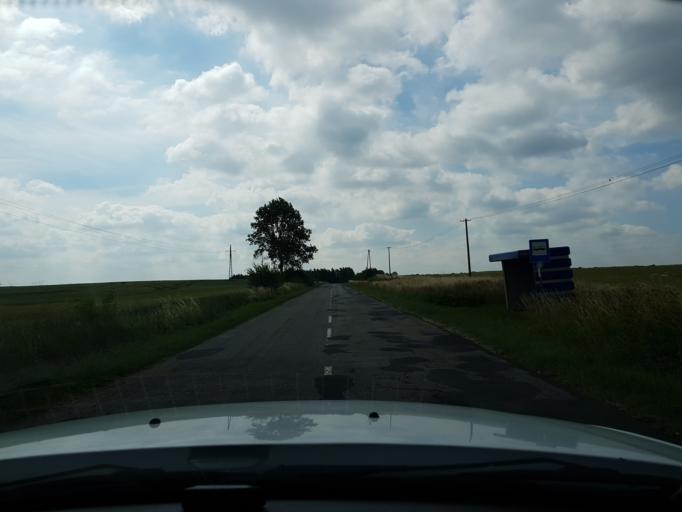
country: PL
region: West Pomeranian Voivodeship
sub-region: Powiat gryfinski
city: Banie
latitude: 53.0830
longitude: 14.6831
